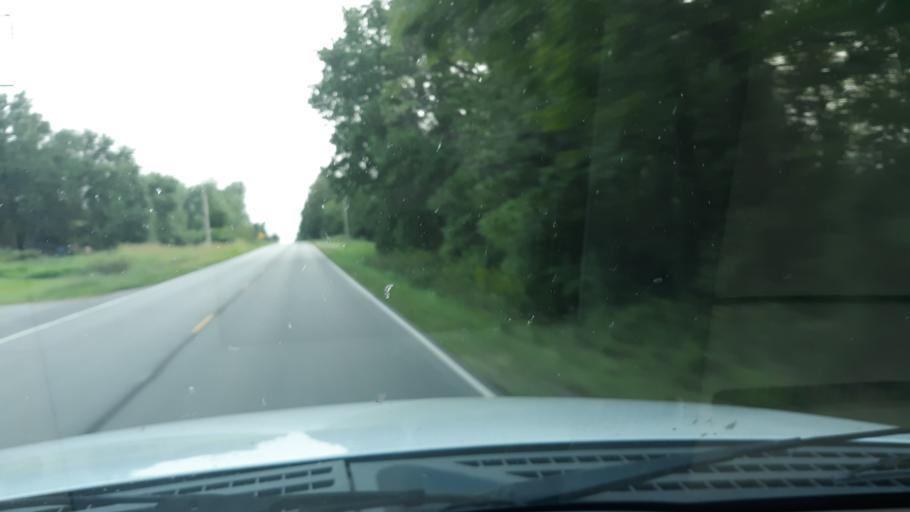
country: US
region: Illinois
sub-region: White County
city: Norris City
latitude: 37.9576
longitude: -88.3361
